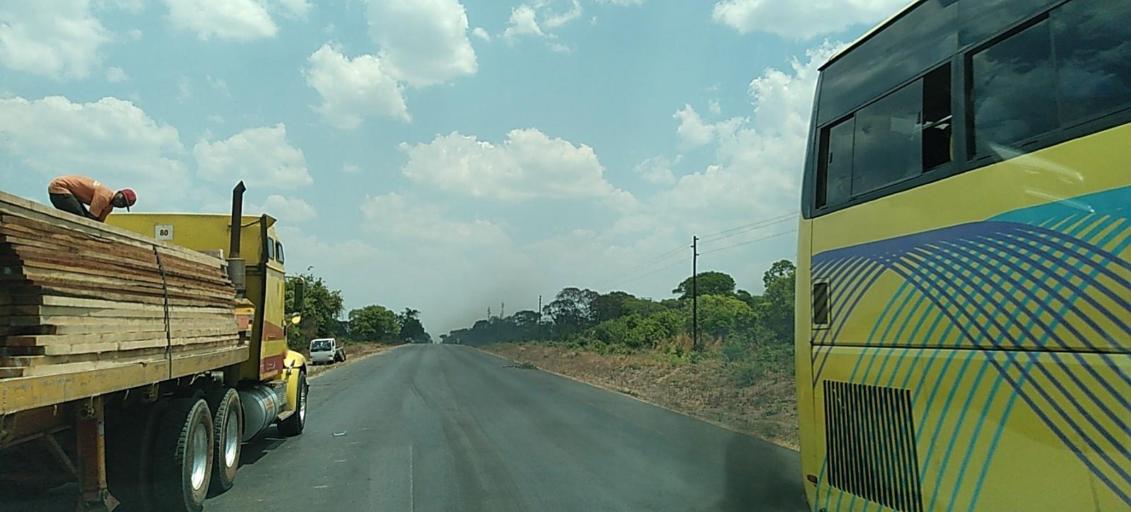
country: ZM
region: Central
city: Kapiri Mposhi
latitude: -14.1169
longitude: 28.6139
